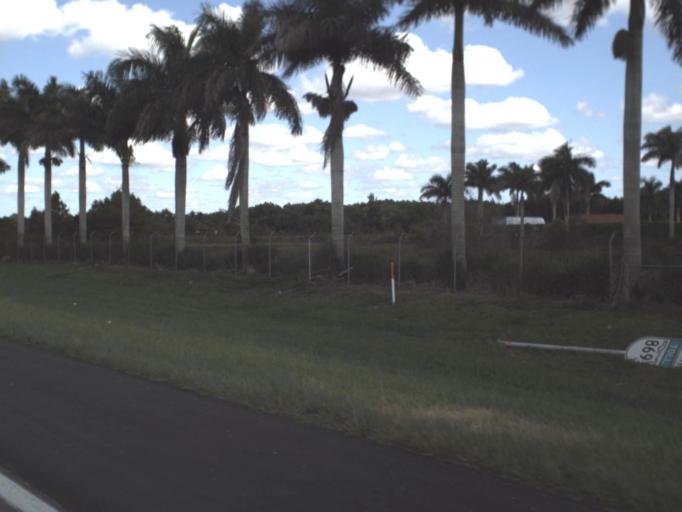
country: US
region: Florida
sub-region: Broward County
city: Tamarac
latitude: 26.2045
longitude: -80.2963
